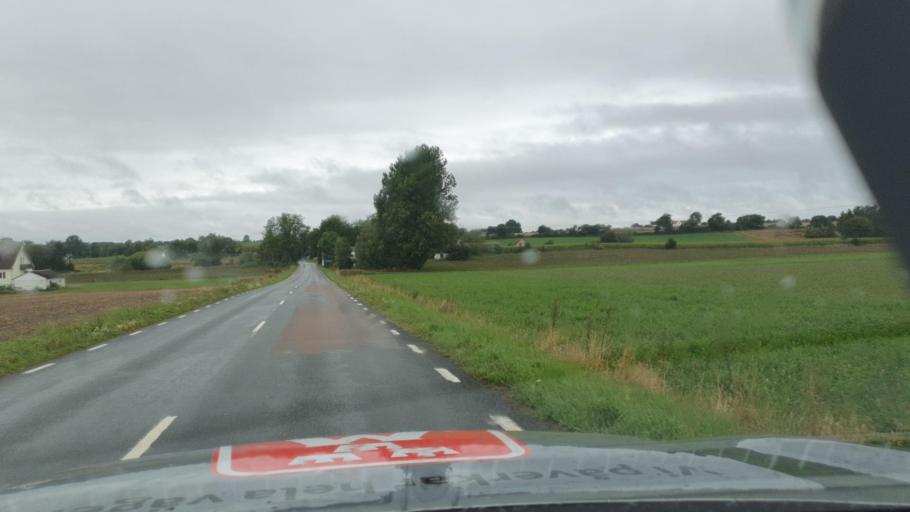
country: SE
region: Skane
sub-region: Simrishamns Kommun
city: Kivik
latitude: 55.5580
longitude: 14.1643
